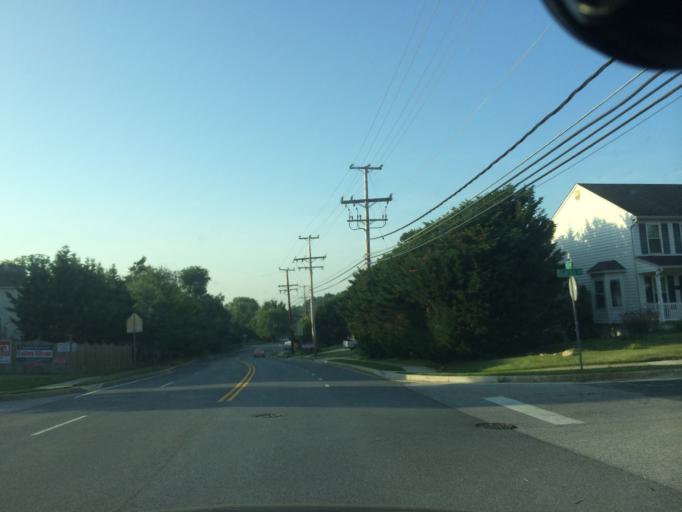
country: US
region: Maryland
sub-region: Carroll County
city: Eldersburg
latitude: 39.3932
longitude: -76.9319
